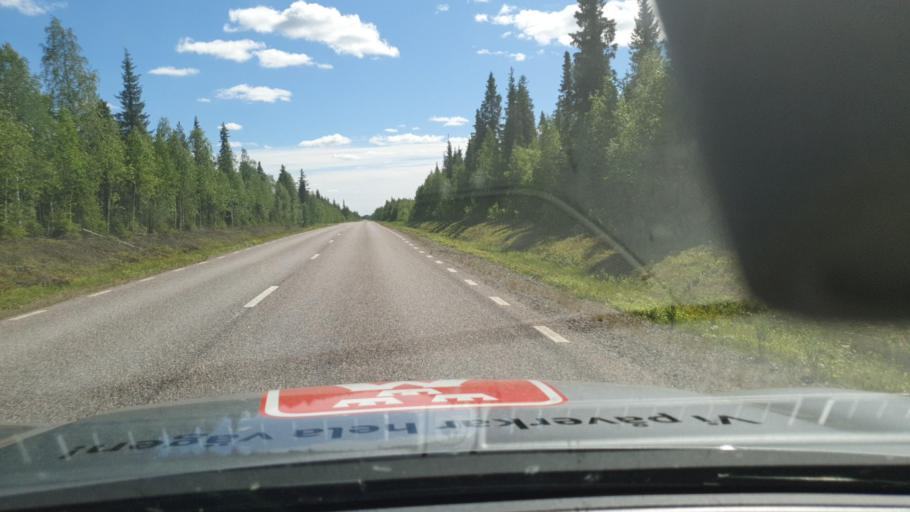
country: SE
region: Norrbotten
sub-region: Pajala Kommun
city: Pajala
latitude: 67.1429
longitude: 23.5710
